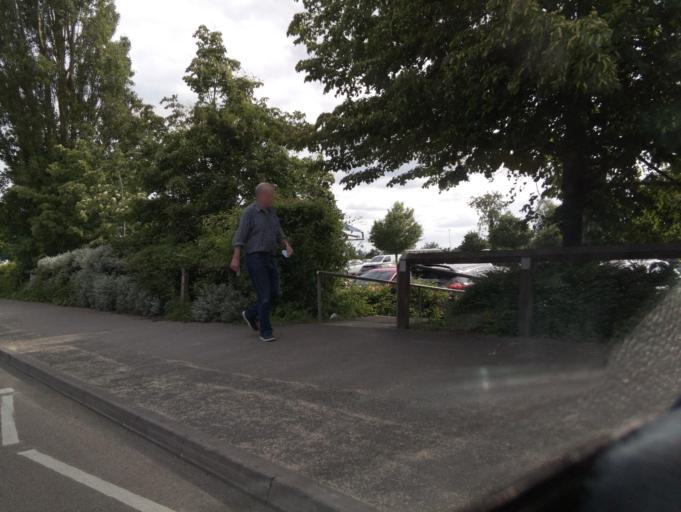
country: GB
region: England
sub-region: Worcestershire
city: Evesham
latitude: 52.1017
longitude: -1.9506
